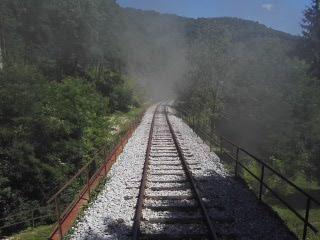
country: SI
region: Kanal
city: Kanal
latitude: 46.0955
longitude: 13.6382
